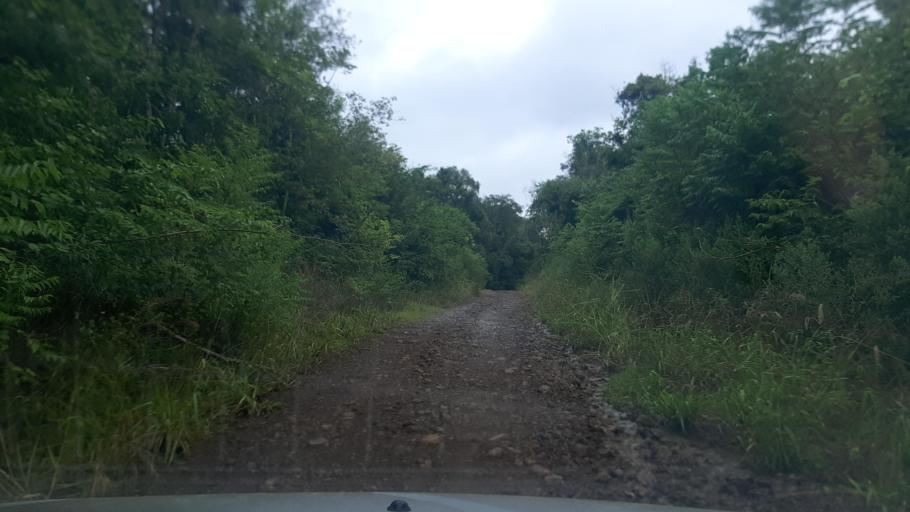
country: BR
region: Parana
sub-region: Ampere
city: Ampere
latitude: -26.0488
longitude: -53.5208
